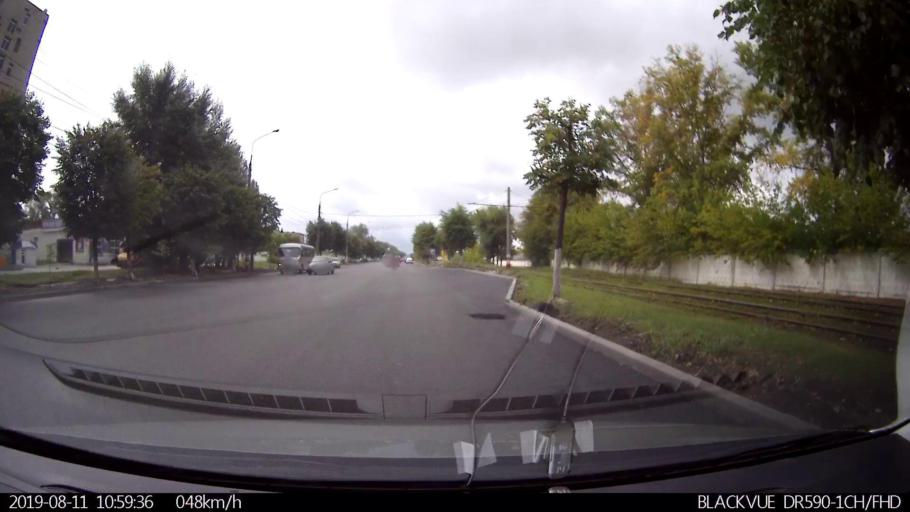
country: RU
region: Ulyanovsk
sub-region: Ulyanovskiy Rayon
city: Ulyanovsk
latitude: 54.2491
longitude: 48.3146
